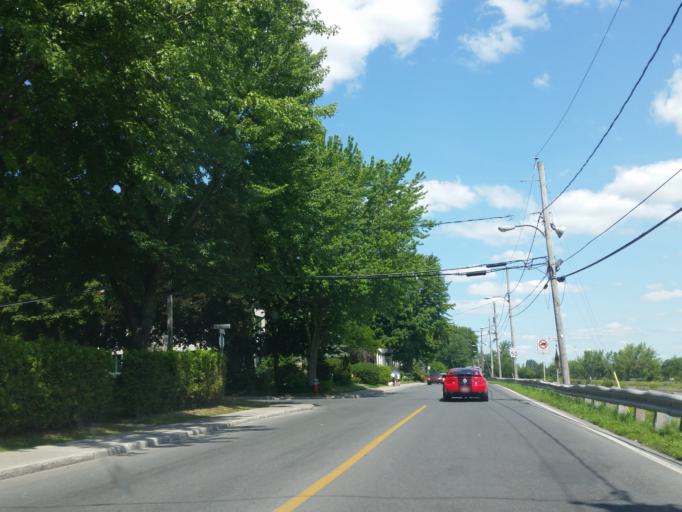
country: CA
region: Quebec
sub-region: Monteregie
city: Saint-Jean-sur-Richelieu
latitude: 45.3126
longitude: -73.2523
